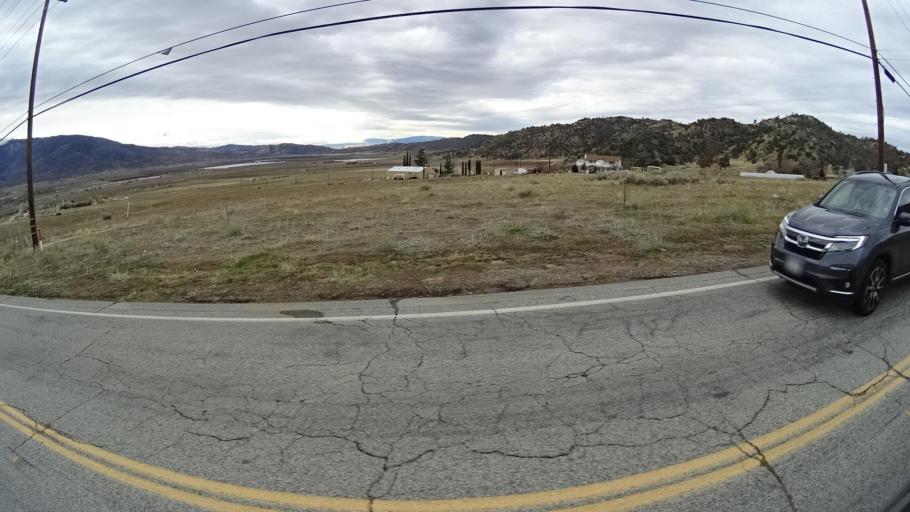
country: US
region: California
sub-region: Kern County
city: Bear Valley Springs
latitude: 35.1460
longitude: -118.5750
